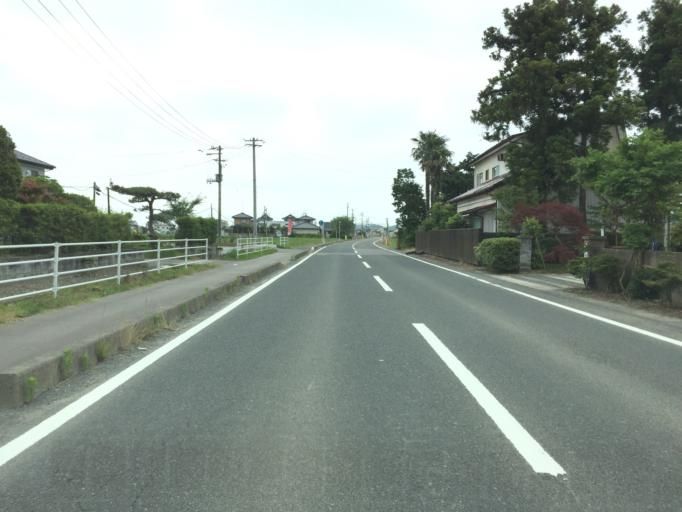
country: JP
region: Fukushima
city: Namie
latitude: 37.6923
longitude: 140.9779
